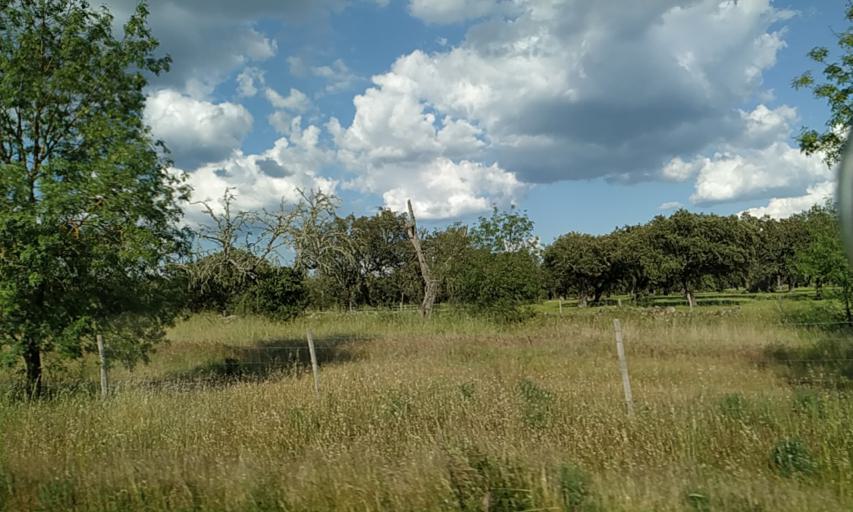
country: PT
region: Portalegre
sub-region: Portalegre
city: Urra
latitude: 39.2094
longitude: -7.4585
